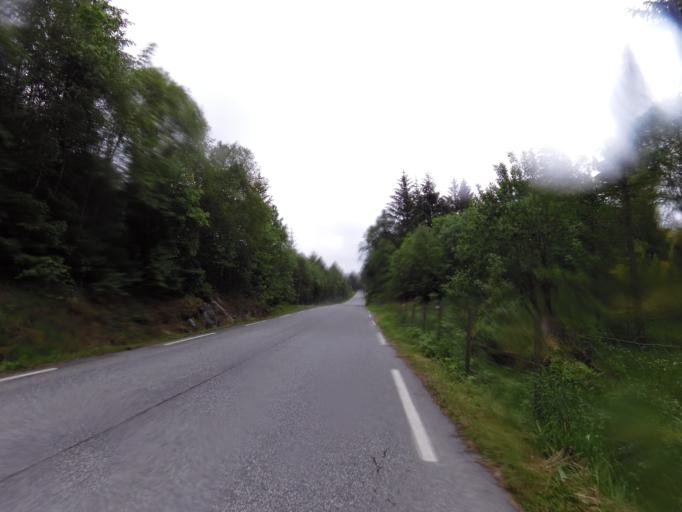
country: NO
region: Hordaland
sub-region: Sveio
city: Sveio
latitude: 59.5230
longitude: 5.2817
